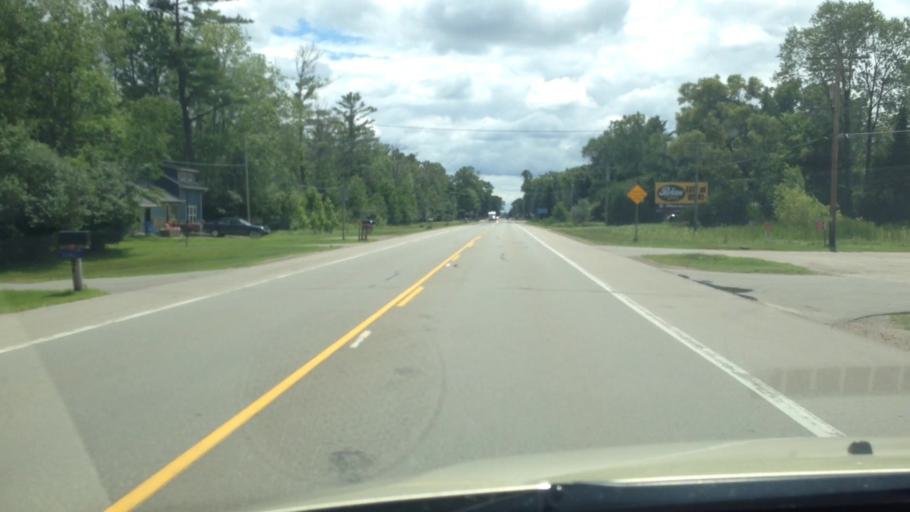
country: US
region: Michigan
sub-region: Menominee County
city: Menominee
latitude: 45.1477
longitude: -87.6030
